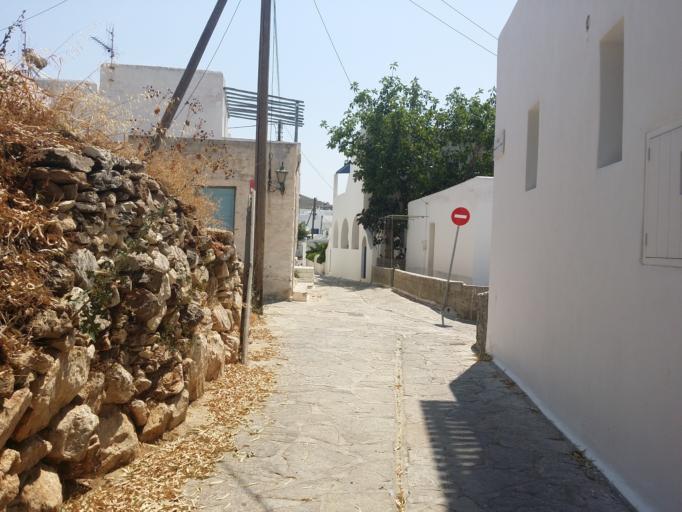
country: GR
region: South Aegean
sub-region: Nomos Kykladon
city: Naousa
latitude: 37.0434
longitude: 25.2476
